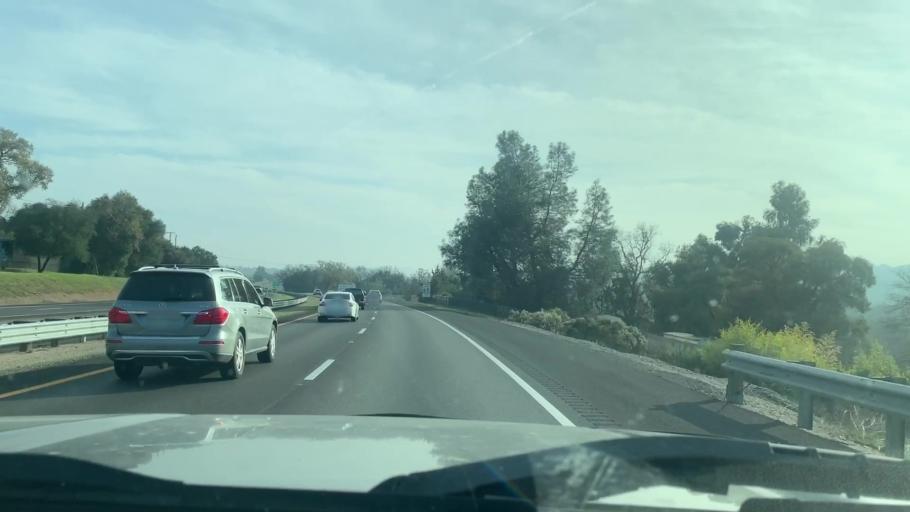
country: US
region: California
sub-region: San Luis Obispo County
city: Templeton
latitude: 35.5202
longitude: -120.7041
